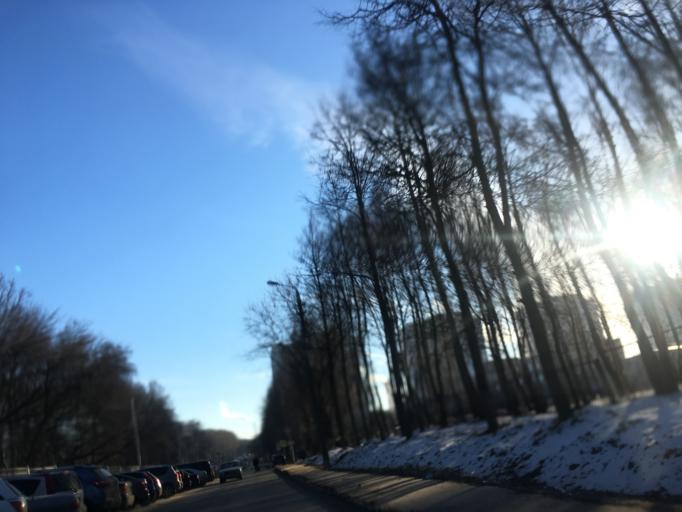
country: RU
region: Tula
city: Mendeleyevskiy
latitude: 54.1773
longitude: 37.5782
